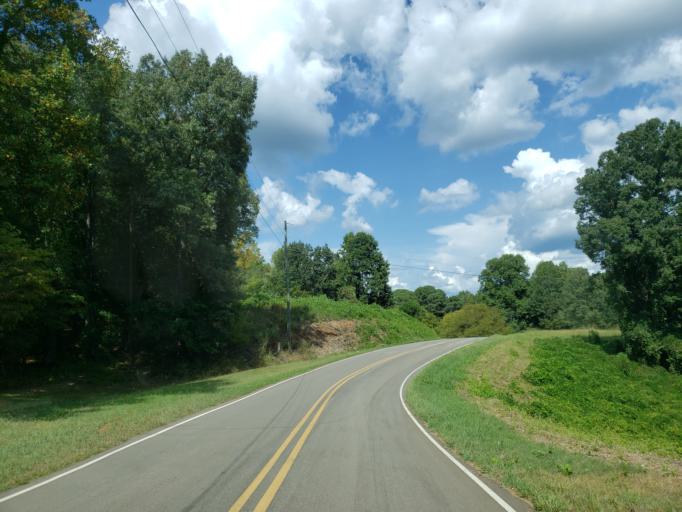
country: US
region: Georgia
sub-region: Pickens County
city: Jasper
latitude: 34.4224
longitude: -84.4423
